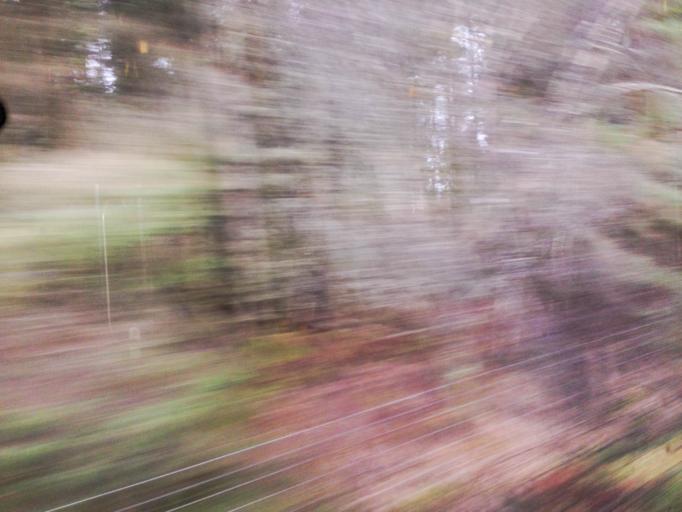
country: GB
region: Scotland
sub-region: Highland
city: Fort William
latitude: 56.8456
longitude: -5.1563
